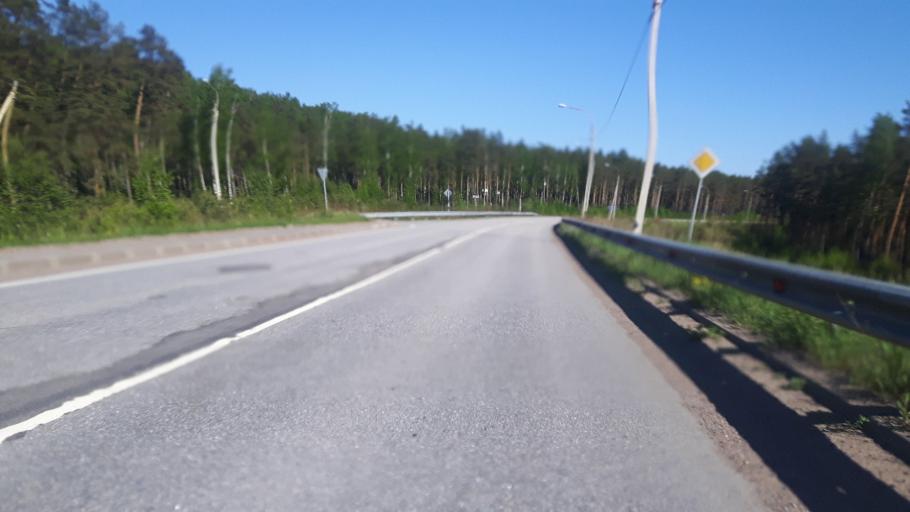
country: RU
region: Leningrad
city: Sosnovyy Bor
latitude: 60.1896
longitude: 29.0185
